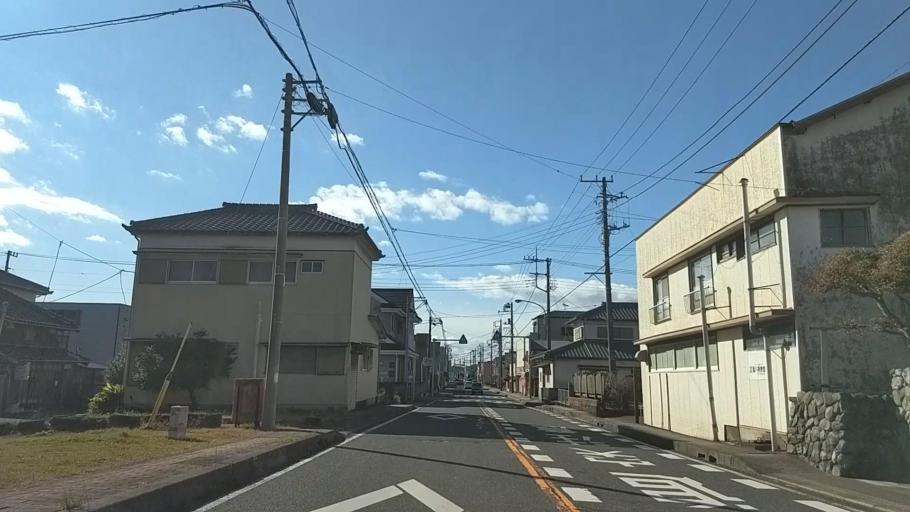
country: JP
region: Chiba
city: Tateyama
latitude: 35.0448
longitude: 139.8352
